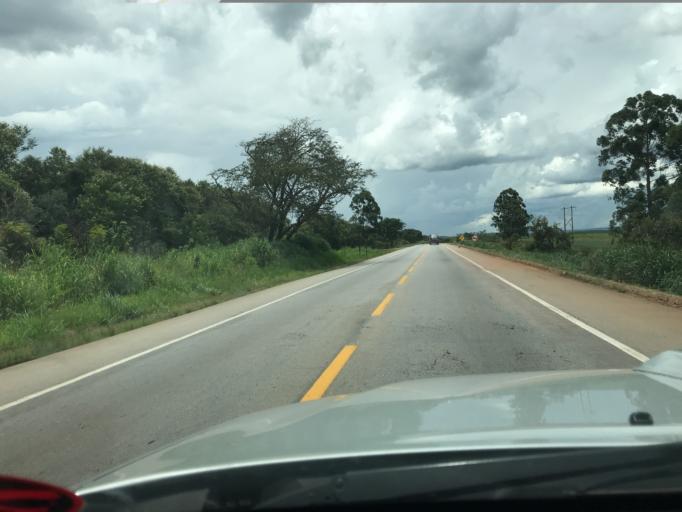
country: BR
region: Minas Gerais
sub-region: Ibia
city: Ibia
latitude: -19.5803
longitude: -46.4511
